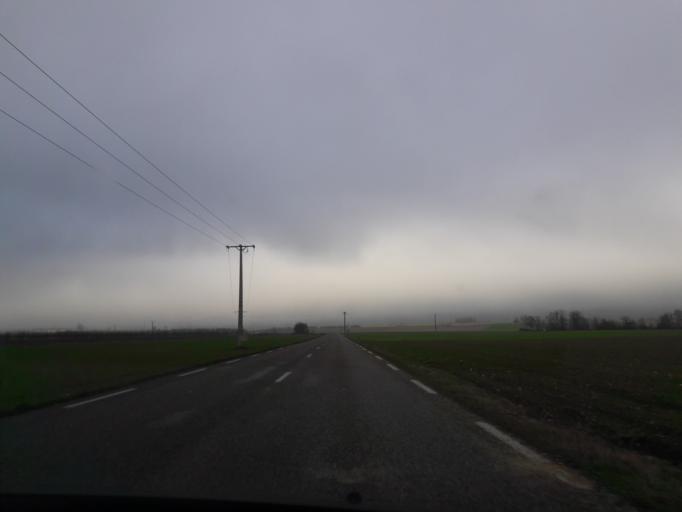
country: FR
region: Rhone-Alpes
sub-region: Departement de l'Isere
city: Gillonnay
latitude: 45.3697
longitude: 5.2889
